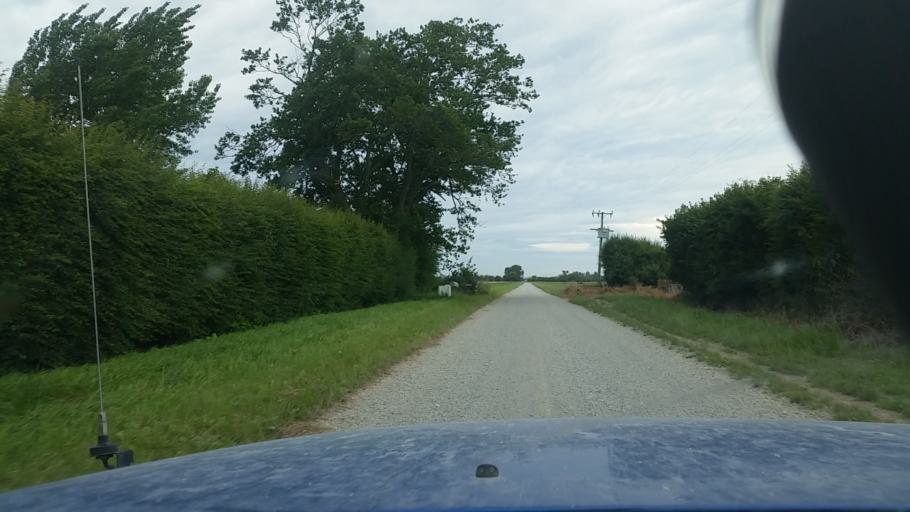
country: NZ
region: Canterbury
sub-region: Ashburton District
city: Ashburton
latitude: -43.8370
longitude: 171.6547
